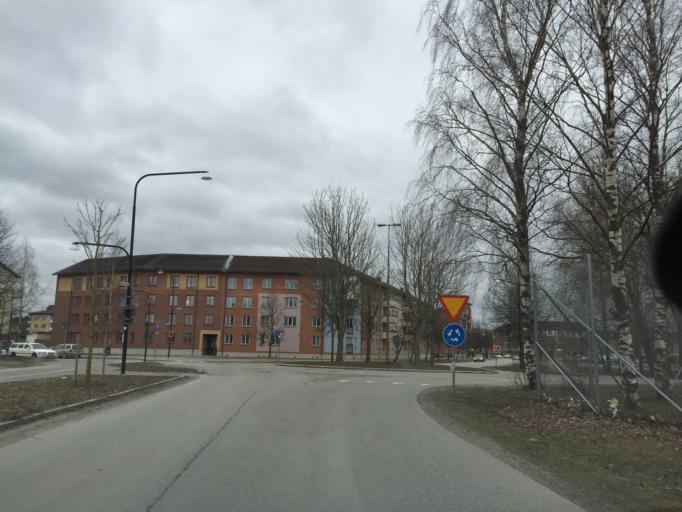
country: SE
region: OErebro
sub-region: Orebro Kommun
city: Orebro
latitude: 59.2590
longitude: 15.2107
